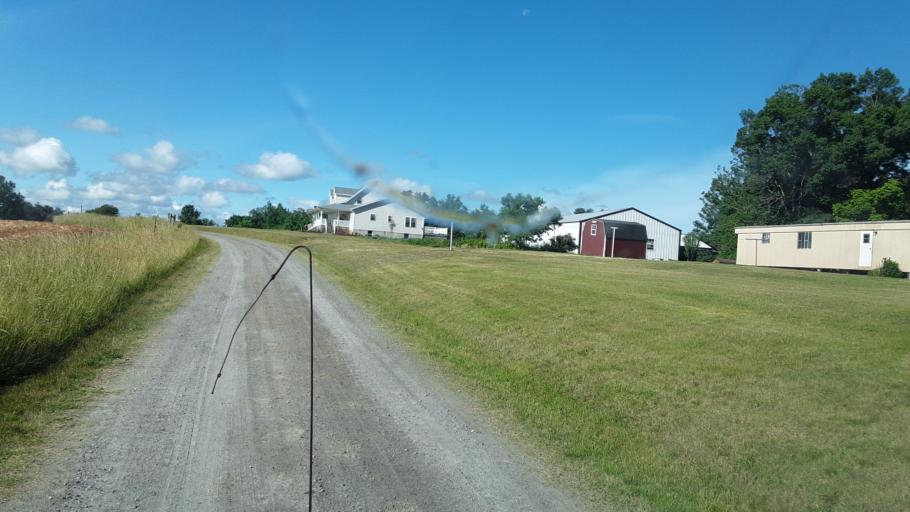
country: US
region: Virginia
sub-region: Pittsylvania County
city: Chatham
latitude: 36.8418
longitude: -79.4157
